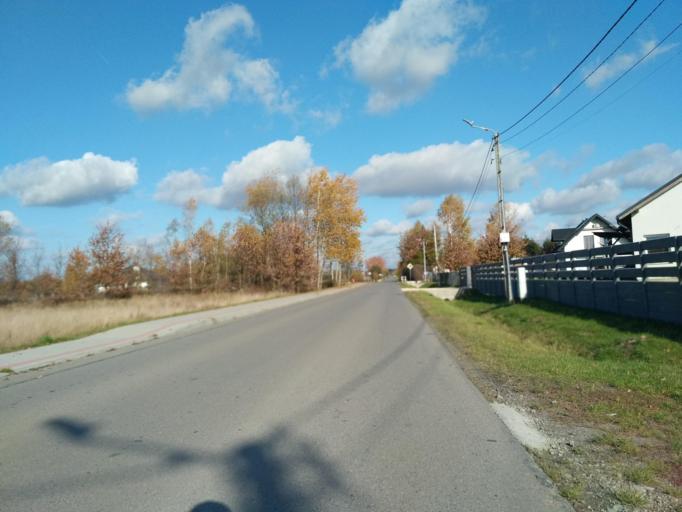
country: PL
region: Subcarpathian Voivodeship
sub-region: Powiat rzeszowski
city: Swilcza
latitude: 50.1196
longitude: 21.8999
